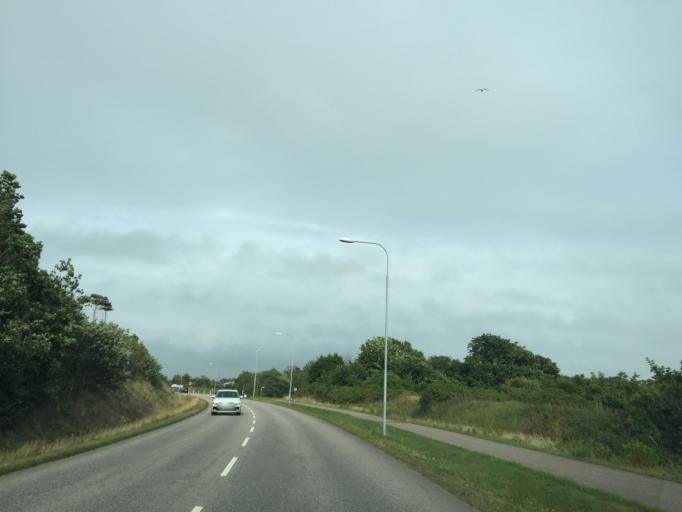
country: SE
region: Halland
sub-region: Falkenbergs Kommun
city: Falkenberg
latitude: 56.8728
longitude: 12.5437
